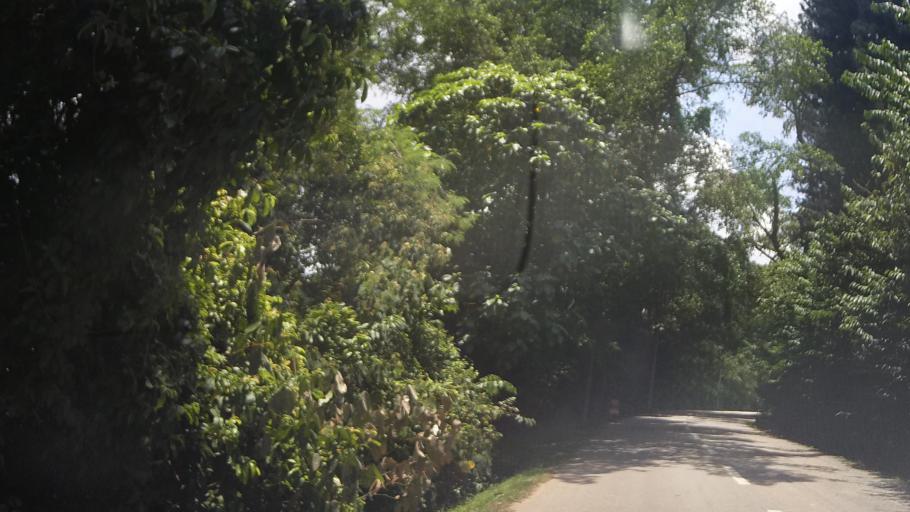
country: MY
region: Johor
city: Kampung Pasir Gudang Baru
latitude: 1.3951
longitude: 103.8668
